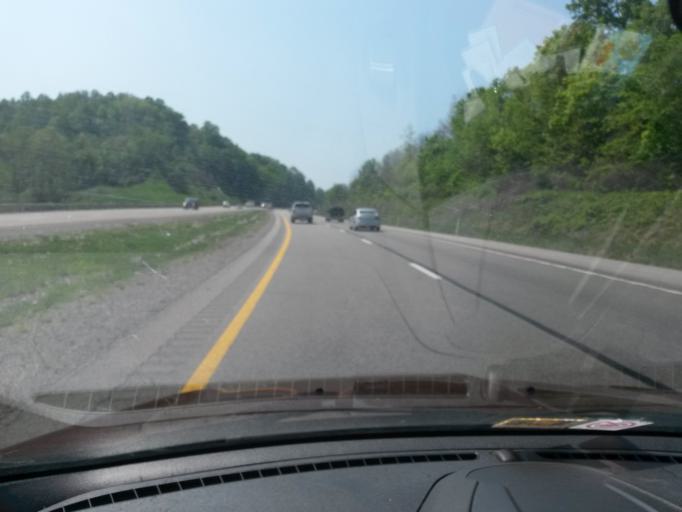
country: US
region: West Virginia
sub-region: Lewis County
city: Weston
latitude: 38.9524
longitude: -80.5349
